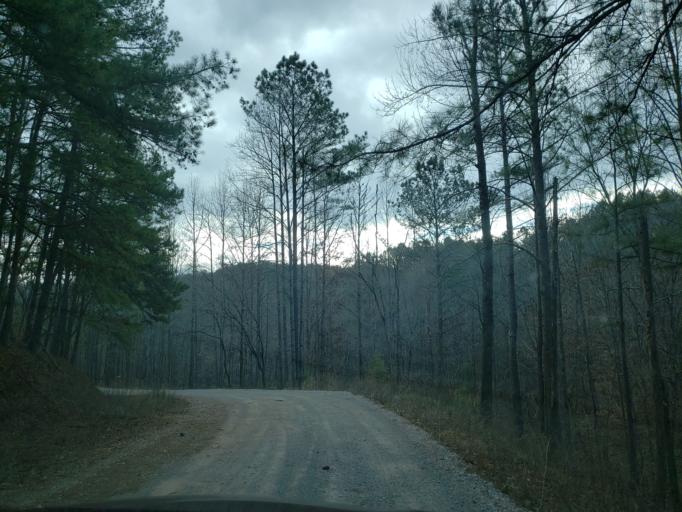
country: US
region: Alabama
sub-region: Cleburne County
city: Heflin
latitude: 33.7090
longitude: -85.6204
